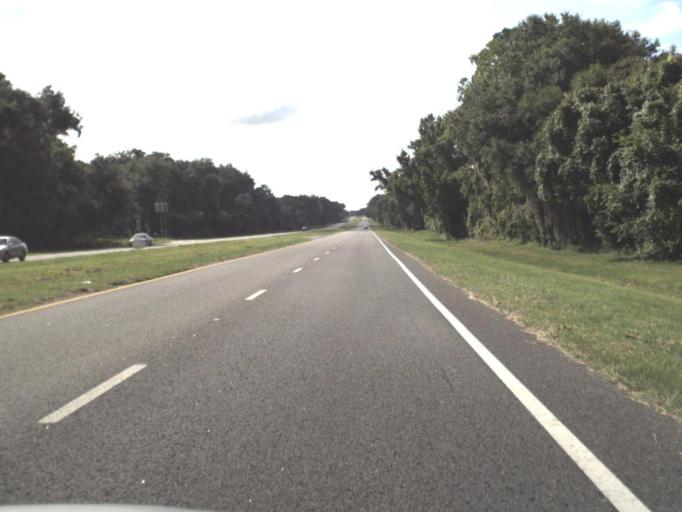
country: US
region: Florida
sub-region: Alachua County
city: Gainesville
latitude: 29.4995
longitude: -82.2623
